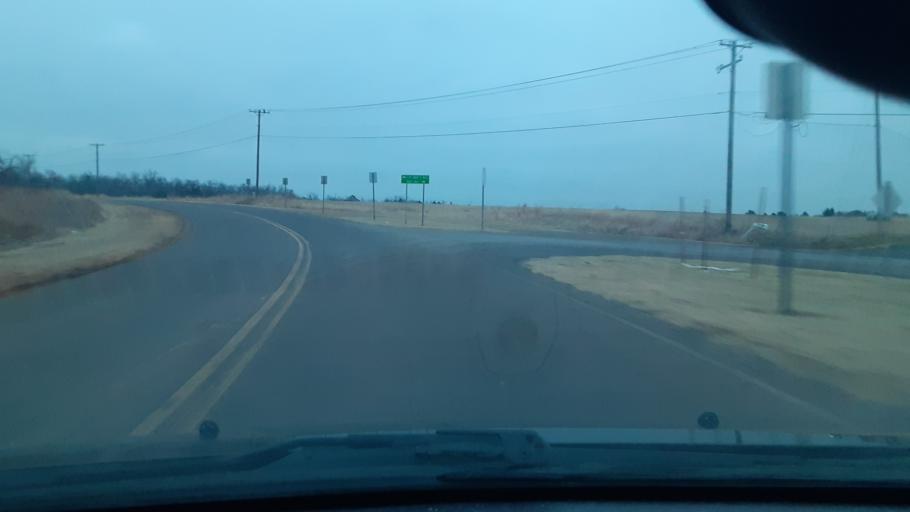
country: US
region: Oklahoma
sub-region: Logan County
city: Guthrie
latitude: 35.8565
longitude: -97.4135
